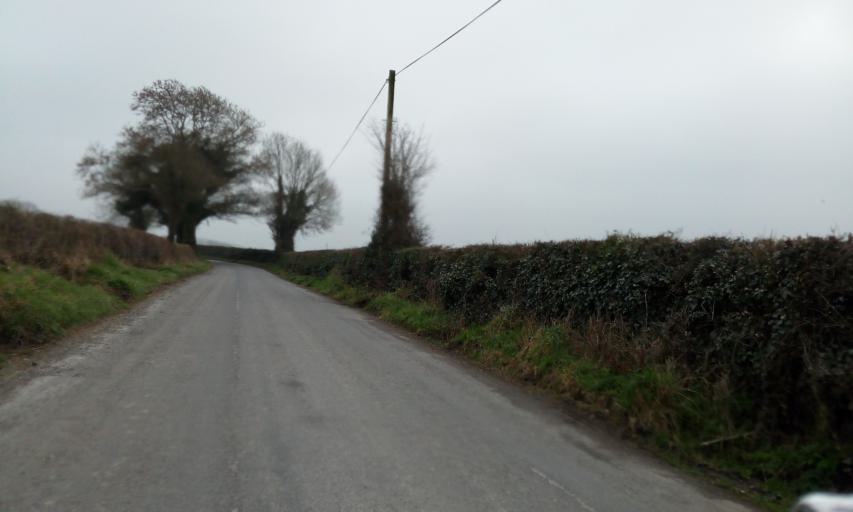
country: IE
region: Leinster
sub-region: Kilkenny
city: Kilkenny
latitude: 52.6574
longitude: -7.1610
